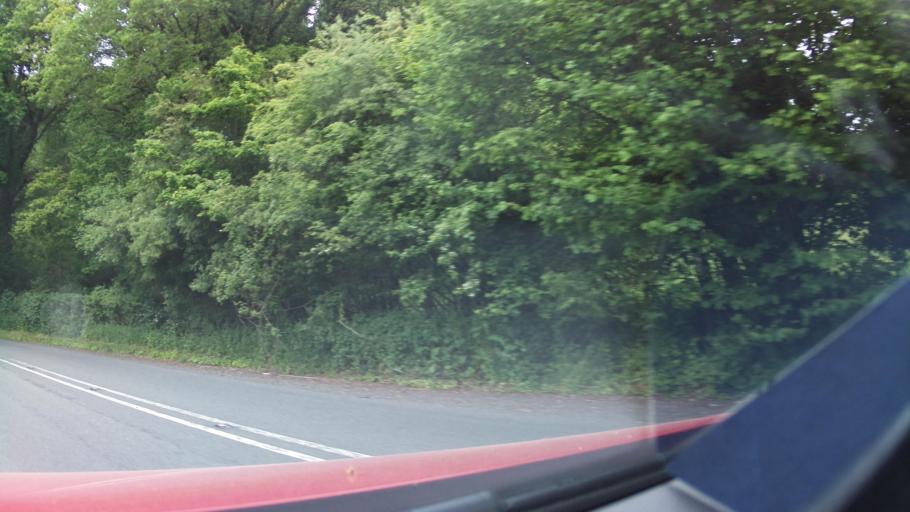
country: GB
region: England
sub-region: Herefordshire
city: Yatton
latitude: 51.9791
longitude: -2.5130
